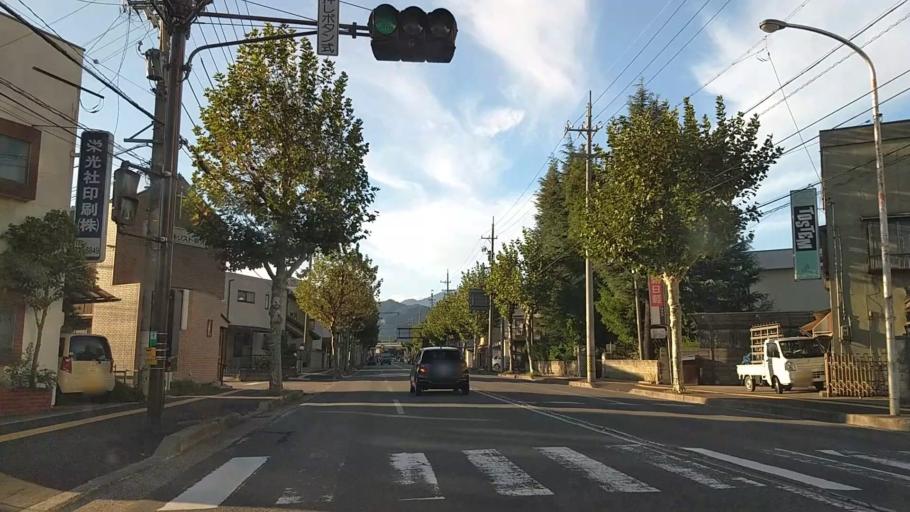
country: JP
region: Nagano
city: Nagano-shi
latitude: 36.6320
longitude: 138.2024
